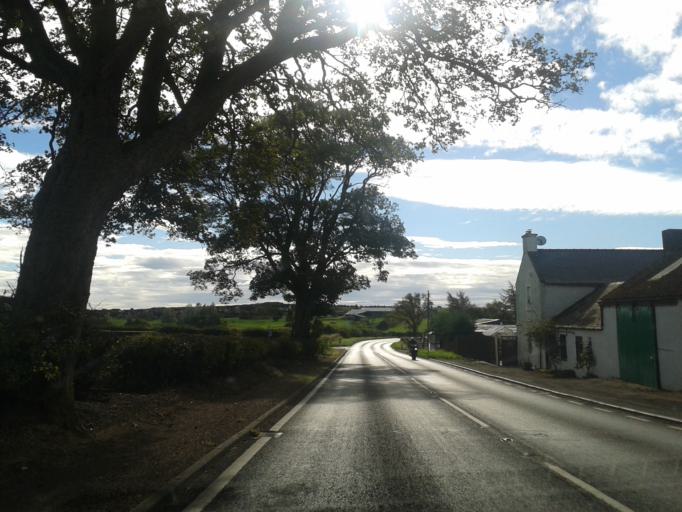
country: GB
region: Scotland
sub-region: Fife
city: Newport-On-Tay
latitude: 56.4215
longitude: -2.9201
